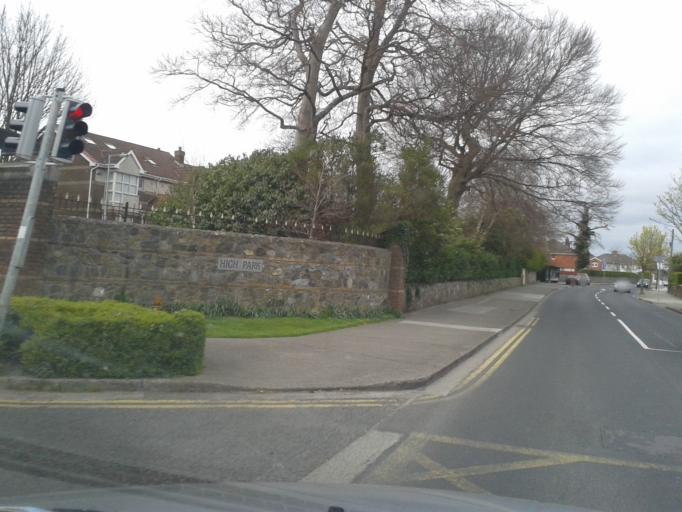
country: IE
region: Leinster
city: Marino
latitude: 53.3792
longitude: -6.2406
